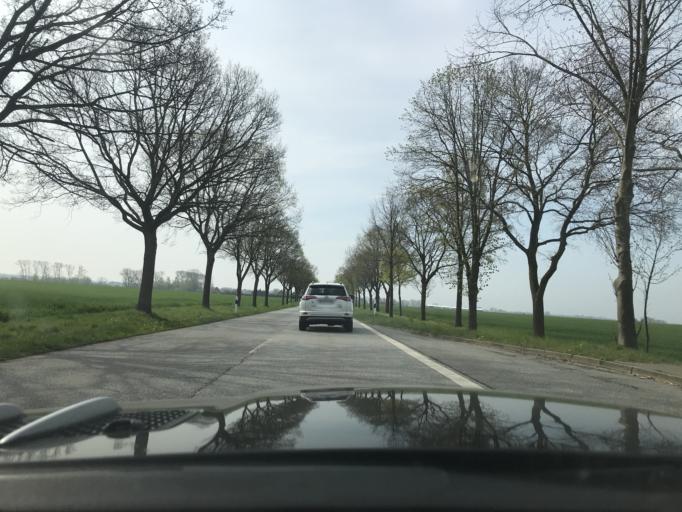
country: DE
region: Schleswig-Holstein
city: Grube
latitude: 54.2529
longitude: 11.0315
